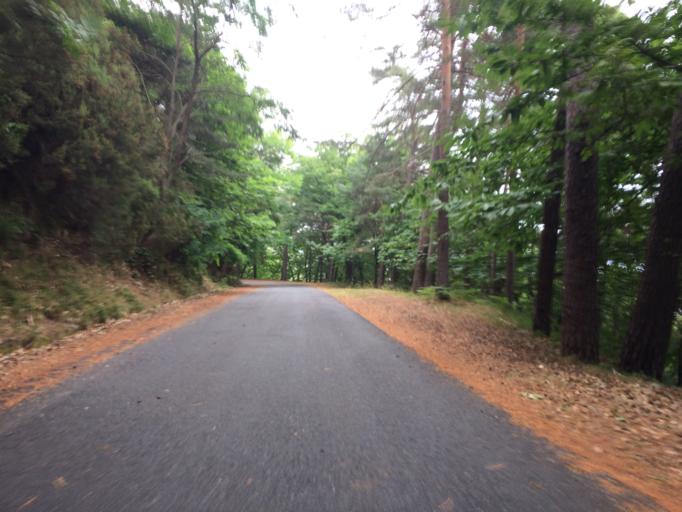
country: IT
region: Liguria
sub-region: Provincia di Imperia
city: Bajardo
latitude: 43.8864
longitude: 7.7336
